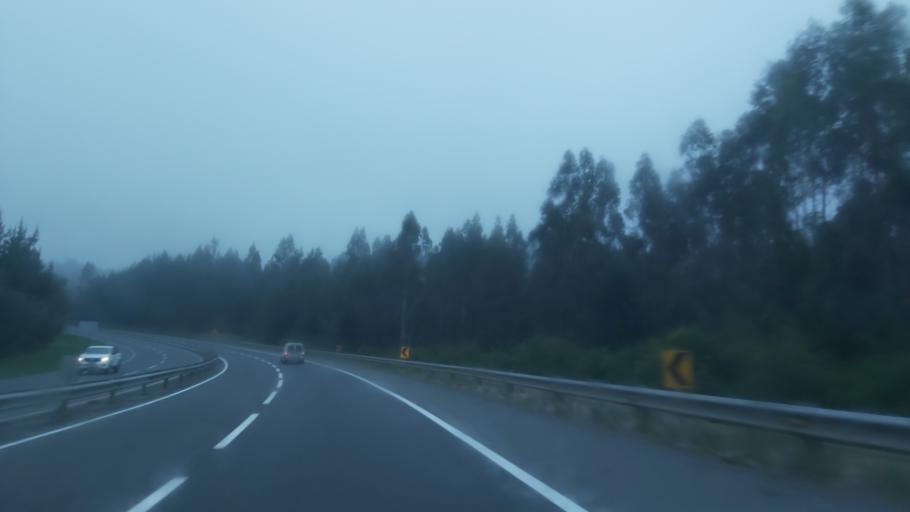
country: CL
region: Biobio
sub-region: Provincia de Concepcion
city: Penco
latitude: -36.7387
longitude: -72.9004
